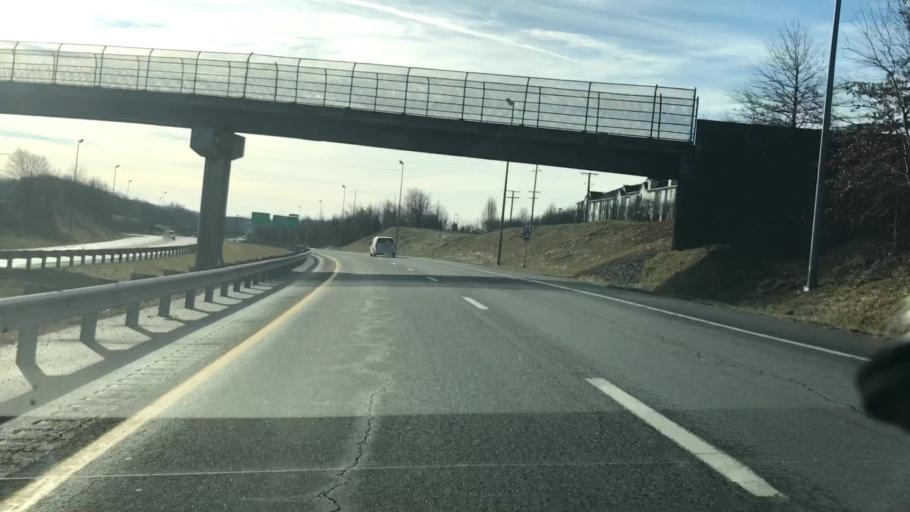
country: US
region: Virginia
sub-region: Montgomery County
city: Merrimac
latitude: 37.1709
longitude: -80.4172
